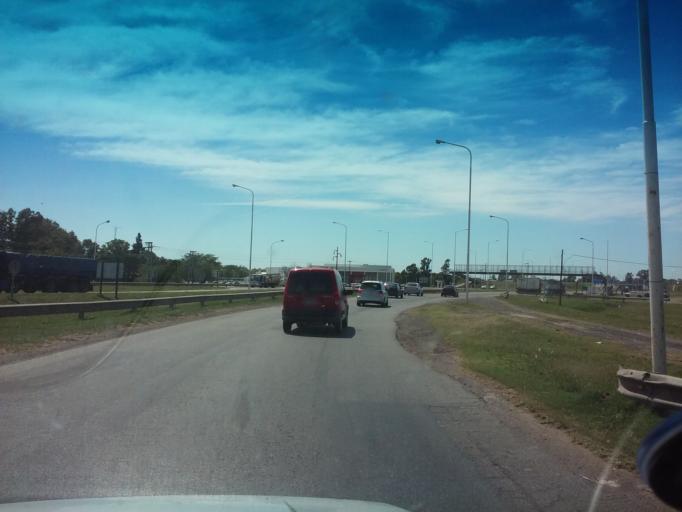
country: AR
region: Buenos Aires
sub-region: Partido de Mercedes
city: Mercedes
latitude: -34.6666
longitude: -59.4068
